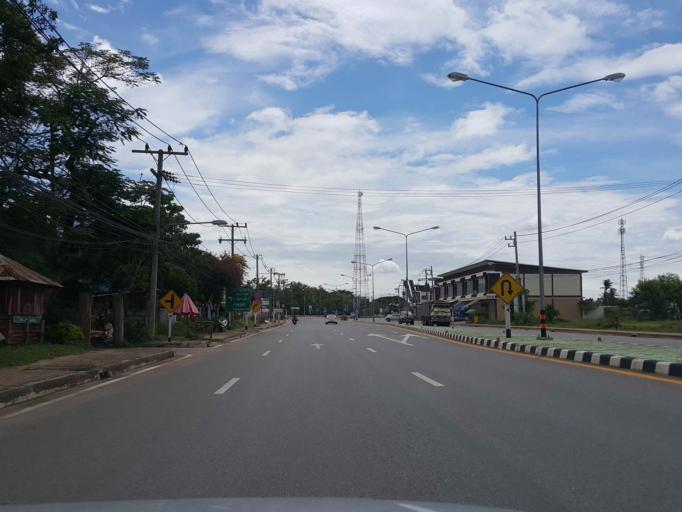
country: TH
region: Sukhothai
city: Ban Dan Lan Hoi
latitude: 17.0081
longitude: 99.5784
